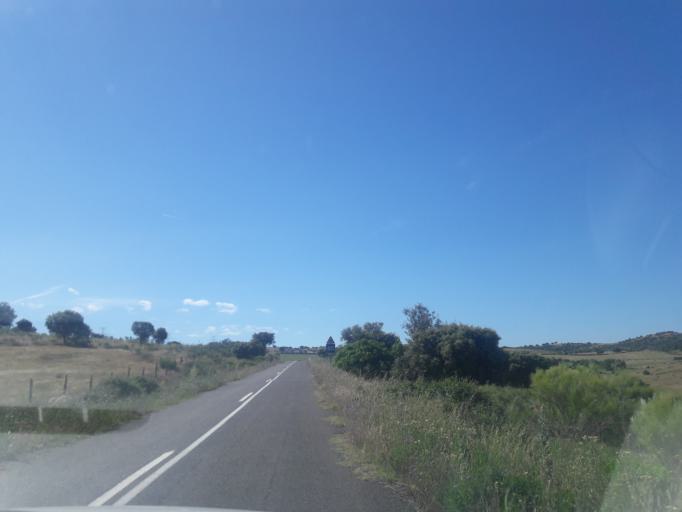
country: ES
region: Castille and Leon
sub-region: Provincia de Salamanca
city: Saucelle
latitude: 40.9983
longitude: -6.7382
